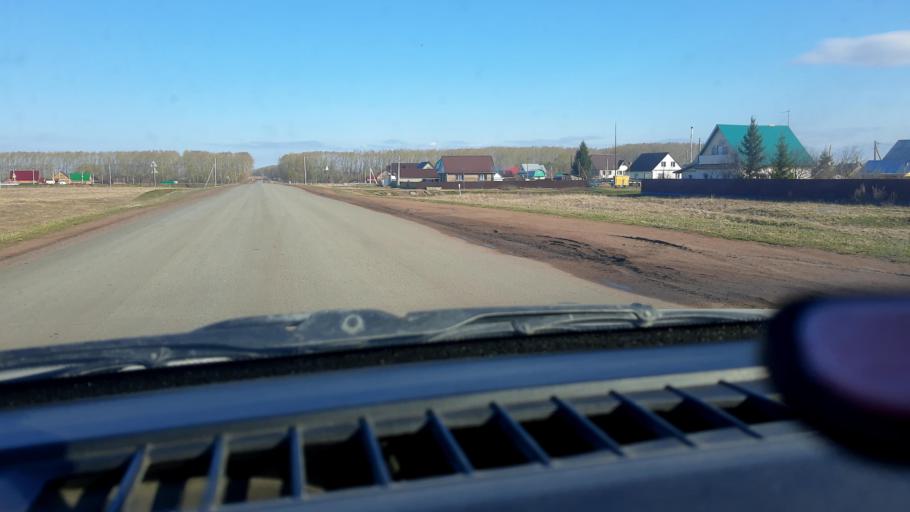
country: RU
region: Bashkortostan
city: Asanovo
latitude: 54.9655
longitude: 55.5444
